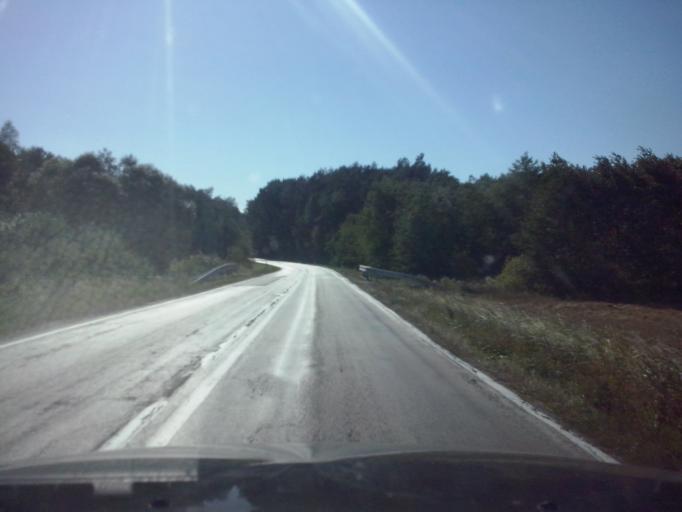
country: PL
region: Swietokrzyskie
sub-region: Powiat kielecki
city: Chmielnik
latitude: 50.6049
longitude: 20.6780
